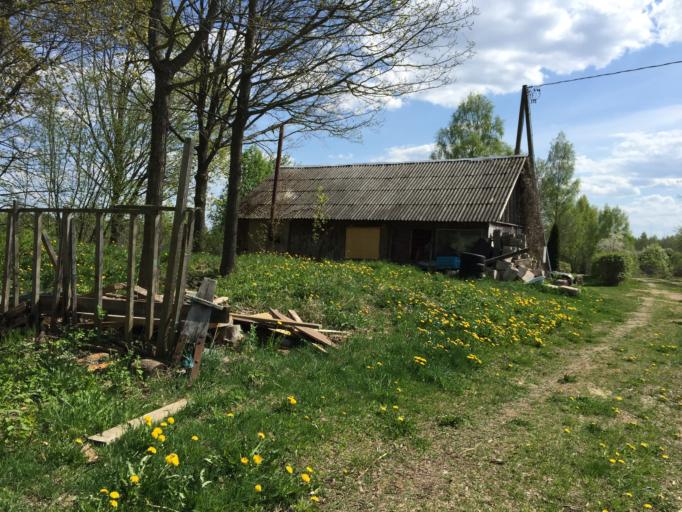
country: LV
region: Limbazu Rajons
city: Limbazi
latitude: 57.3524
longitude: 24.6589
